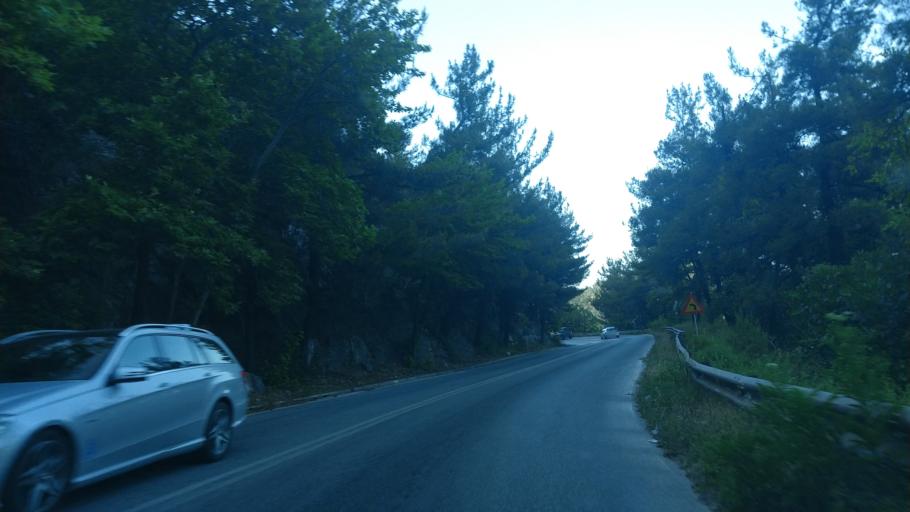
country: GR
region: East Macedonia and Thrace
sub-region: Nomos Kavalas
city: Potamia
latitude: 40.7256
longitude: 24.7325
